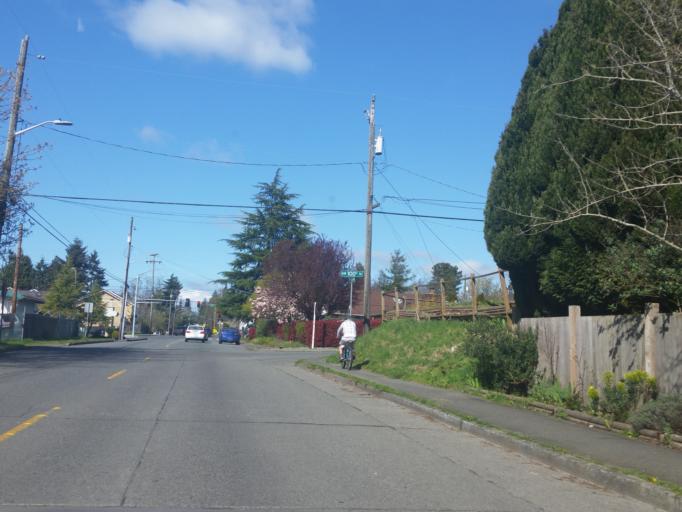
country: US
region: Washington
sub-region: King County
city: Shoreline
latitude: 47.7012
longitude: -122.3608
